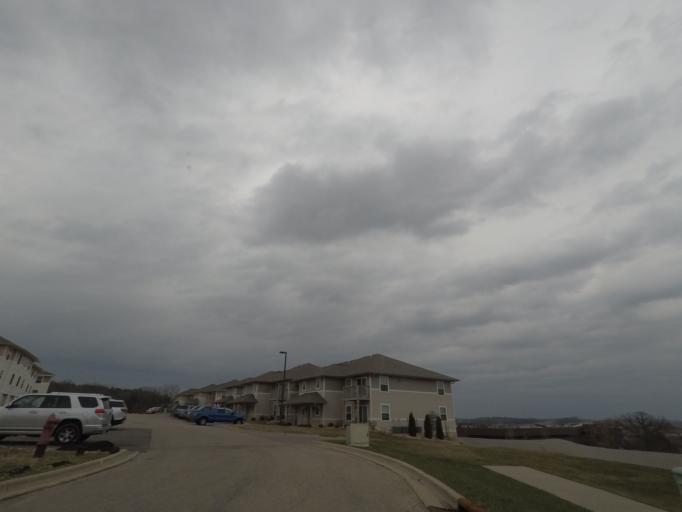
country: US
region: Wisconsin
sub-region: Dane County
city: Middleton
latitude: 43.1070
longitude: -89.5378
